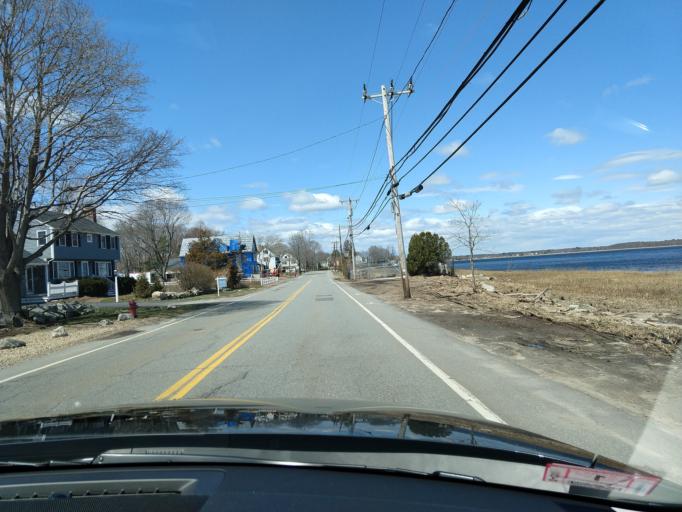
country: US
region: Massachusetts
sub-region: Essex County
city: Newburyport
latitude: 42.8005
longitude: -70.8503
